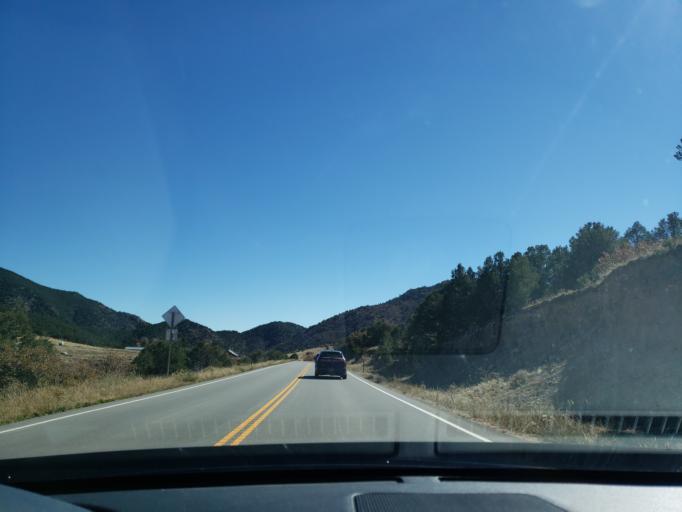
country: US
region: Colorado
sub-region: Fremont County
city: Canon City
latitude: 38.5874
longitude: -105.4212
